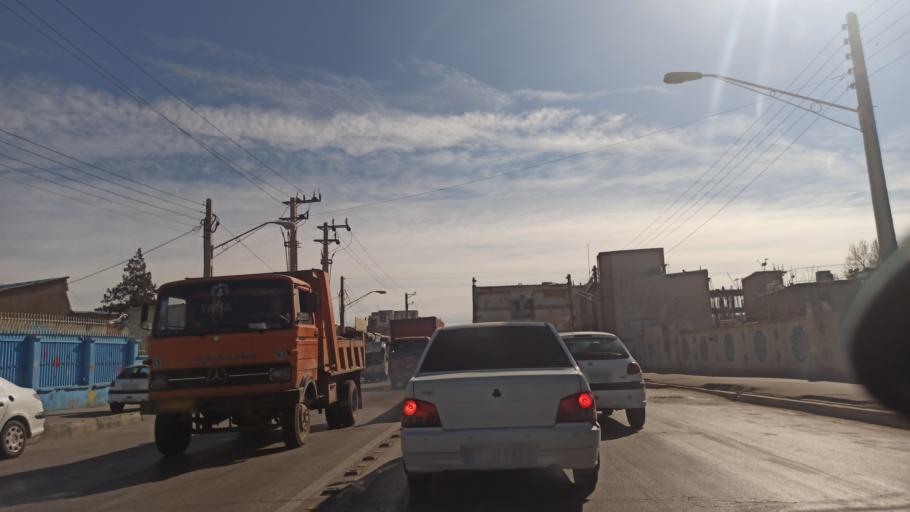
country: IR
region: Qazvin
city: Qazvin
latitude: 36.2524
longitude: 50.0010
